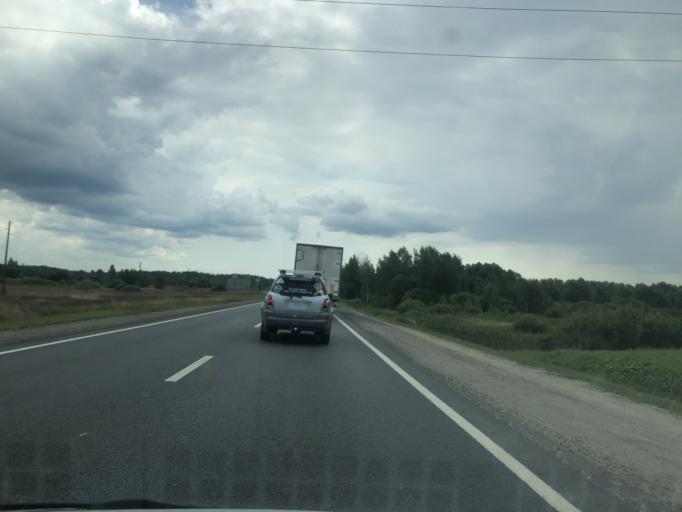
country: RU
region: Jaroslavl
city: Pereslavl'-Zalesskiy
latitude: 56.7812
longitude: 38.8847
